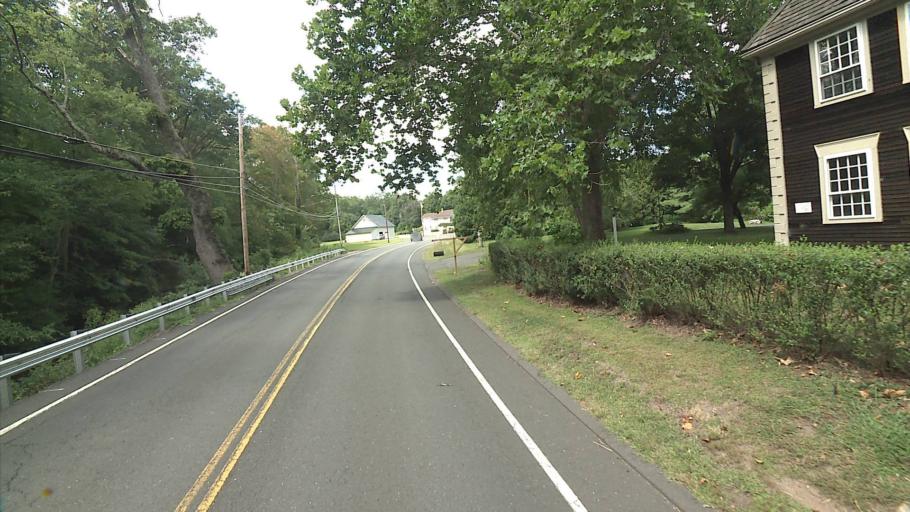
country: US
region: Connecticut
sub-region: Hartford County
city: North Granby
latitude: 42.0017
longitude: -72.8371
